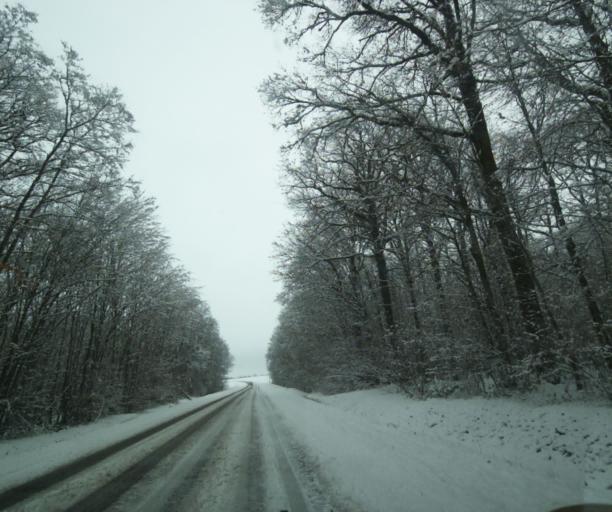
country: FR
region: Champagne-Ardenne
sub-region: Departement de la Haute-Marne
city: Montier-en-Der
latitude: 48.5254
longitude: 4.7992
